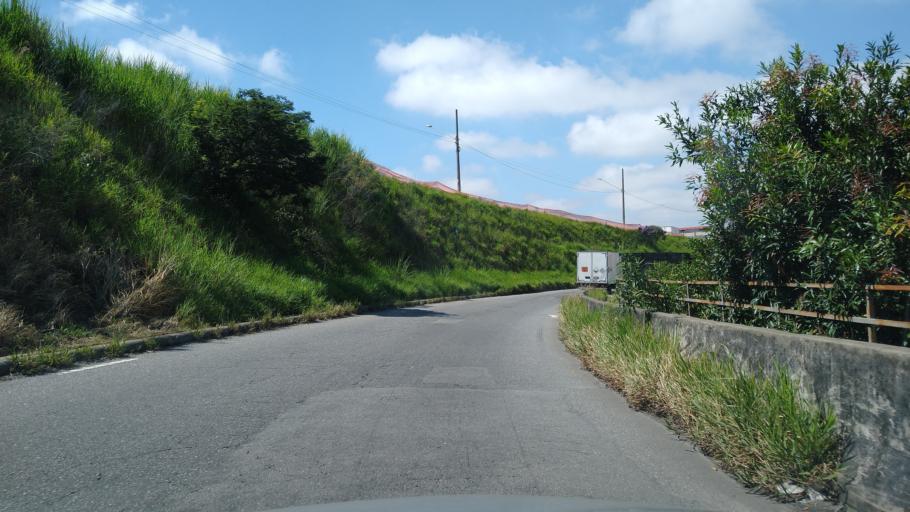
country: BR
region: Sao Paulo
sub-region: Guarulhos
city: Guarulhos
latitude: -23.4562
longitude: -46.4738
